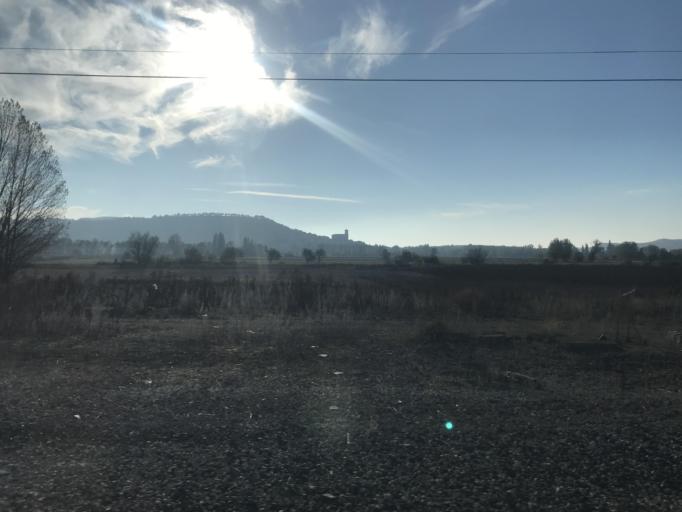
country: ES
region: Castille and Leon
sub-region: Provincia de Burgos
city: Villaquiran de los Infantes
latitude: 42.2146
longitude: -4.0021
